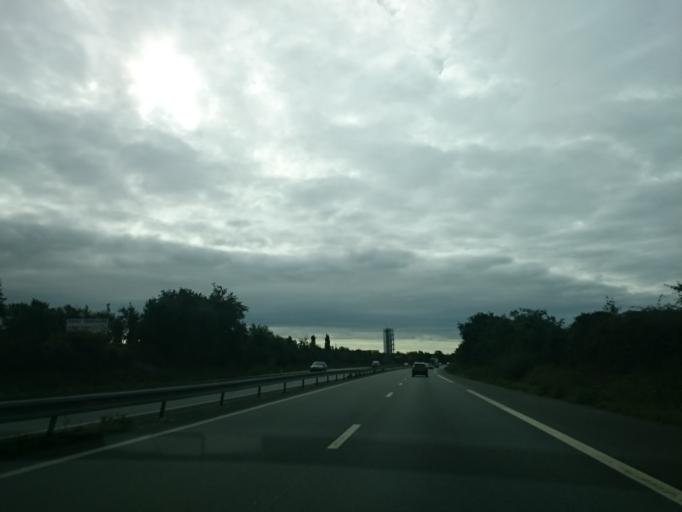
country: FR
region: Brittany
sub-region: Departement du Morbihan
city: Auray
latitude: 47.6711
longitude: -3.0147
